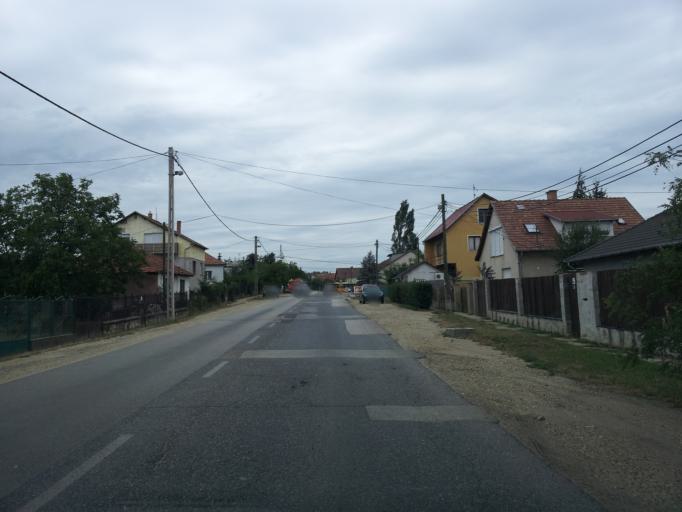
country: HU
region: Pest
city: Erd
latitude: 47.4088
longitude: 18.8824
